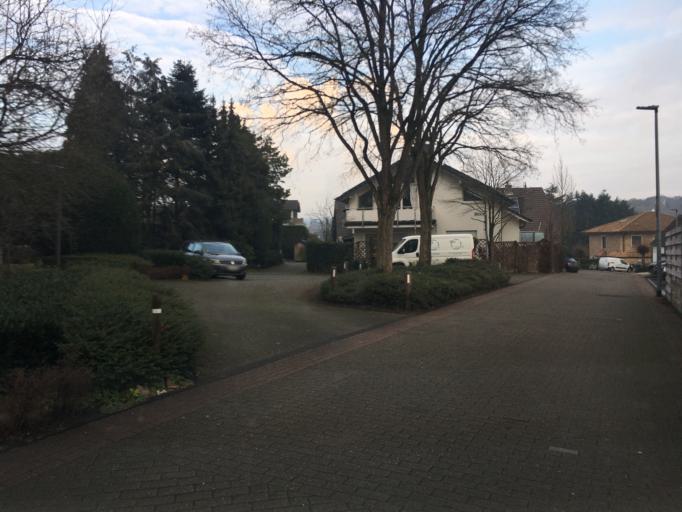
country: DE
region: North Rhine-Westphalia
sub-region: Regierungsbezirk Koln
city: Odenthal
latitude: 51.0186
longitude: 7.0981
